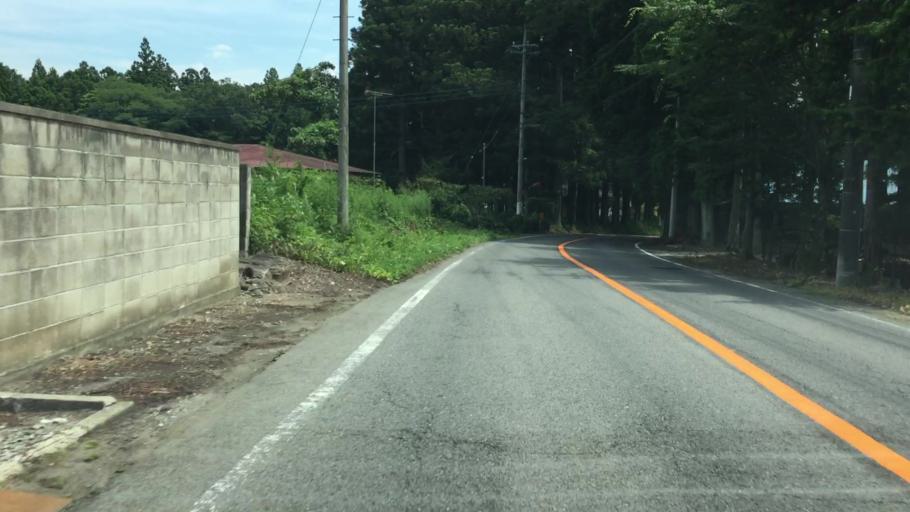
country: JP
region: Tochigi
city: Kuroiso
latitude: 37.0355
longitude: 139.9425
